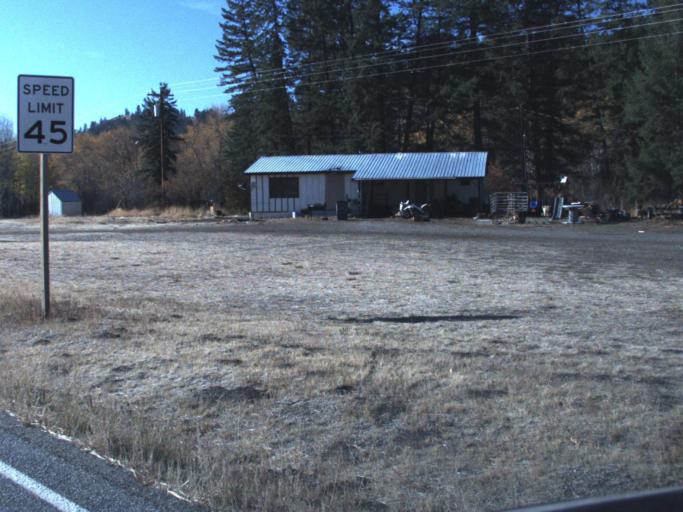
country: US
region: Washington
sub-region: Ferry County
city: Republic
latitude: 48.8065
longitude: -118.6025
